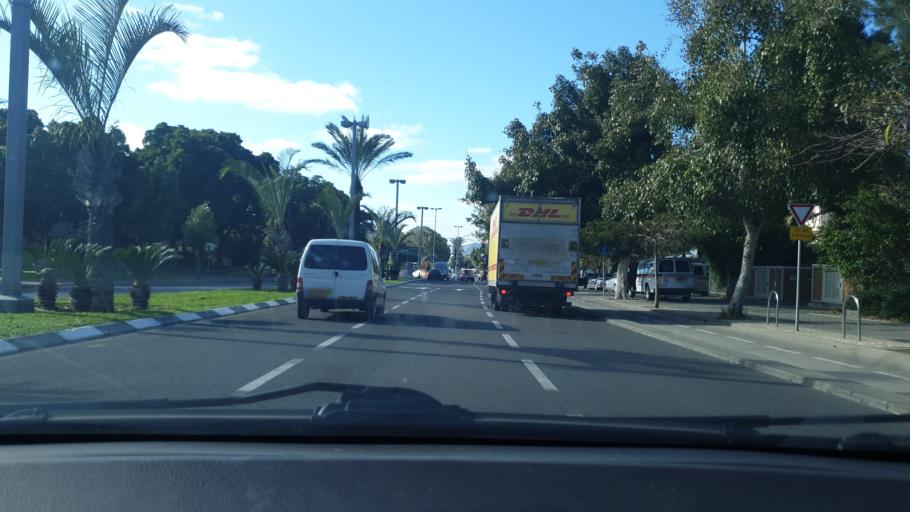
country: IL
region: Tel Aviv
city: Yafo
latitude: 32.0443
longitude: 34.7690
